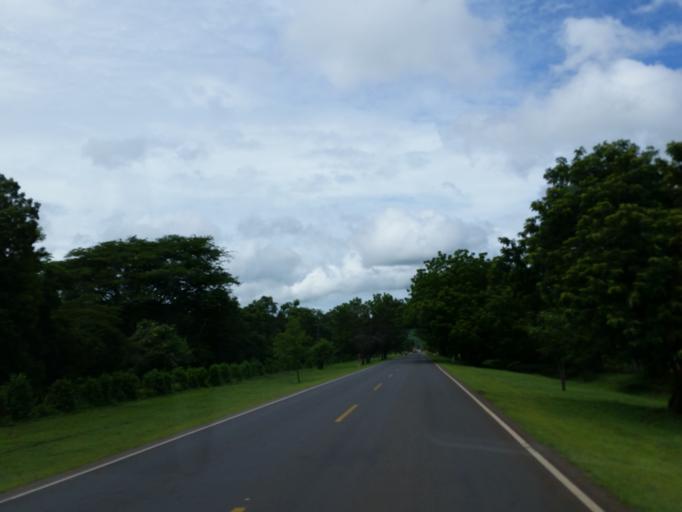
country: NI
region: Leon
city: Telica
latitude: 12.5917
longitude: -86.7302
